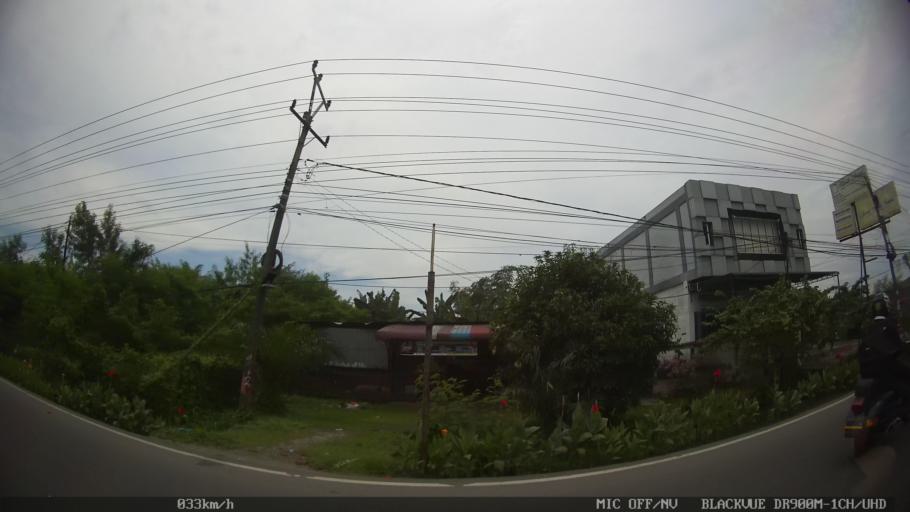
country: ID
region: North Sumatra
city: Sunggal
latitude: 3.5995
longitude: 98.5589
